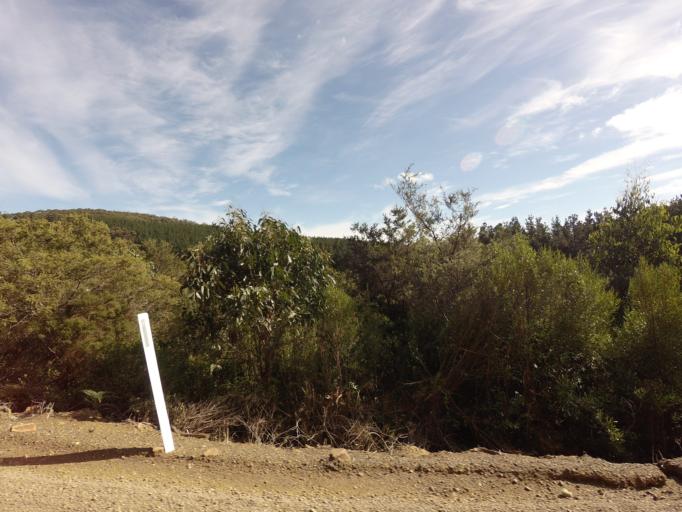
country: AU
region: Tasmania
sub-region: Clarence
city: Sandford
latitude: -43.1805
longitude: 147.7708
